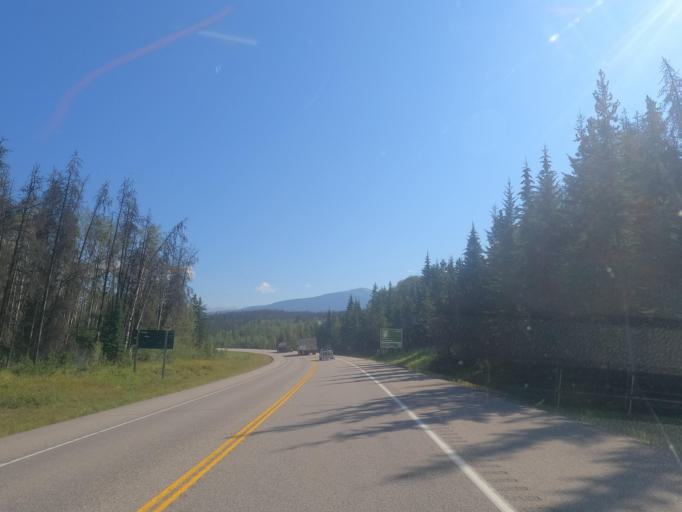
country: CA
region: Alberta
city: Jasper Park Lodge
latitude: 52.8575
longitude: -118.1199
